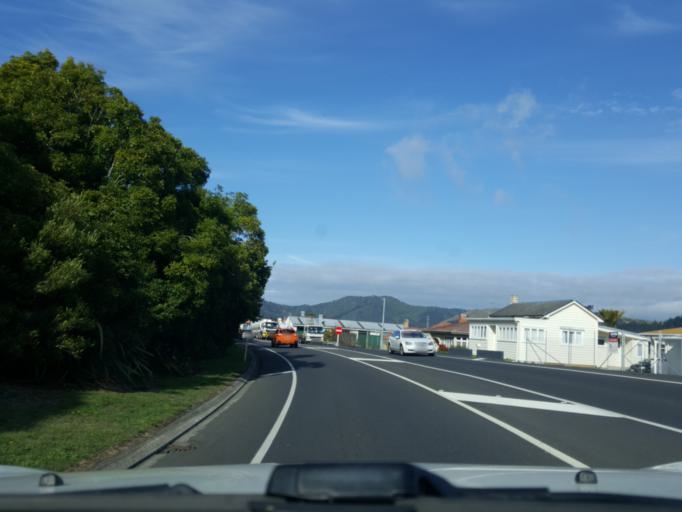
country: NZ
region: Waikato
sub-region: Waikato District
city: Ngaruawahia
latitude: -37.5700
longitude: 175.1581
